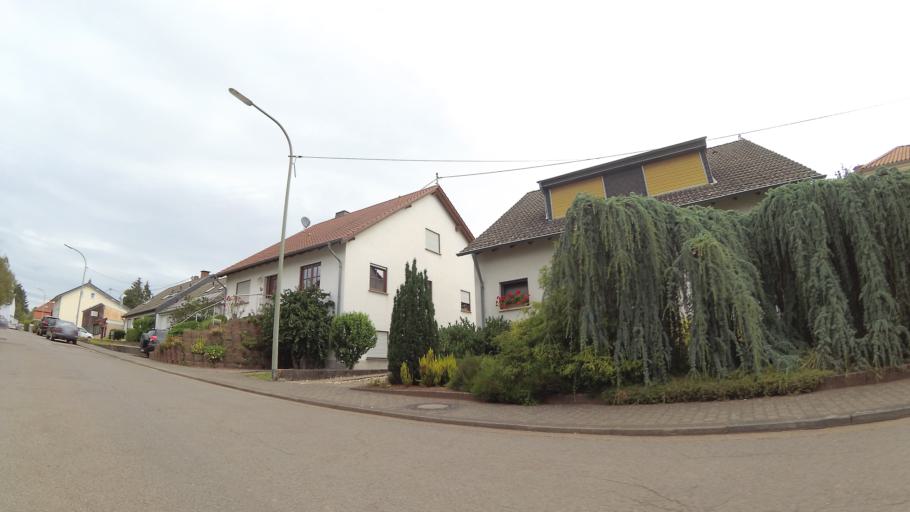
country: DE
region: Saarland
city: Schwalbach
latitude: 49.3161
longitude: 6.8075
